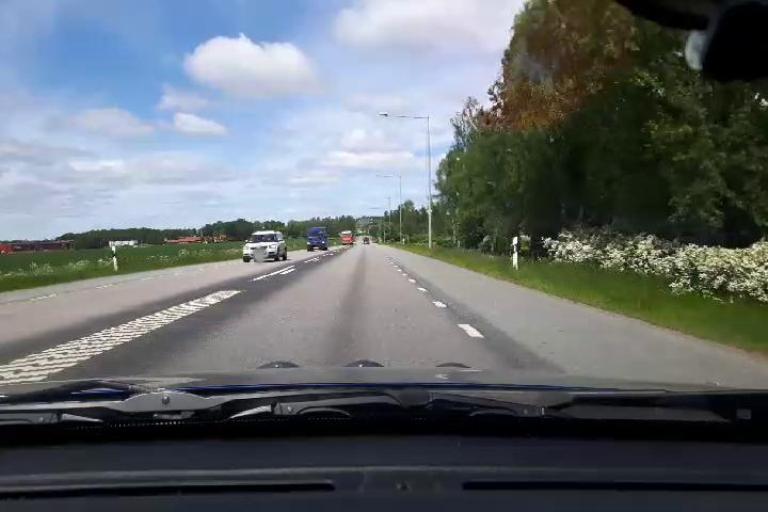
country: SE
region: Uppsala
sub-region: Osthammars Kommun
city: Bjorklinge
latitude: 60.0200
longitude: 17.5557
